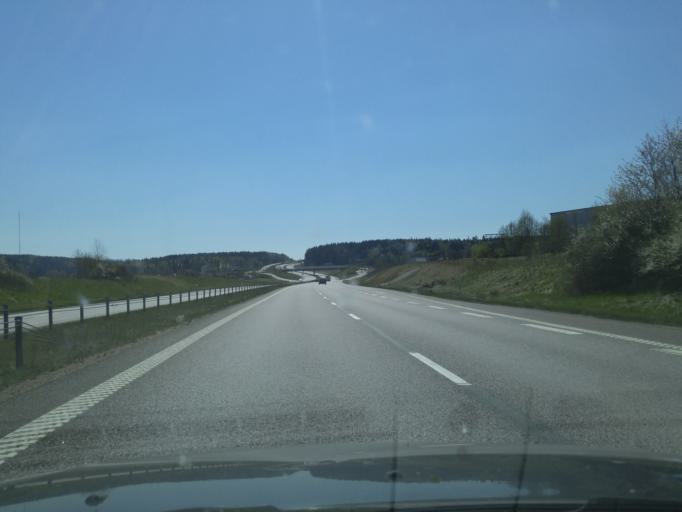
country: SE
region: Vaestra Goetaland
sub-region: Munkedals Kommun
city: Munkedal
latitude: 58.3972
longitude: 11.7513
